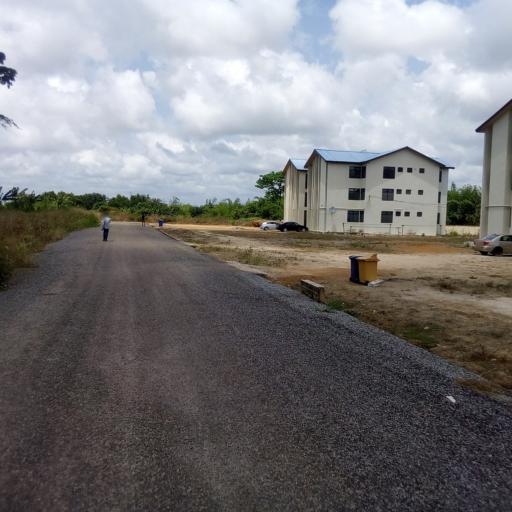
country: GH
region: Central
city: Cape Coast
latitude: 5.1333
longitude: -1.2962
